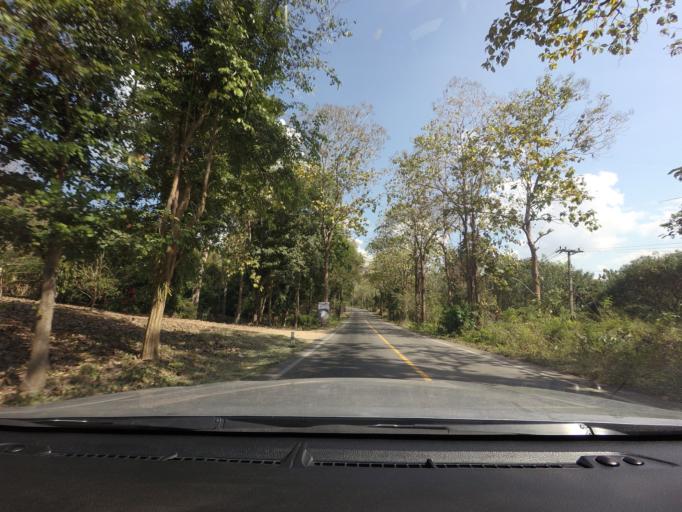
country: TH
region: Chiang Mai
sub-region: Amphoe Chiang Dao
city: Chiang Dao
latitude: 19.4490
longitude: 98.9844
